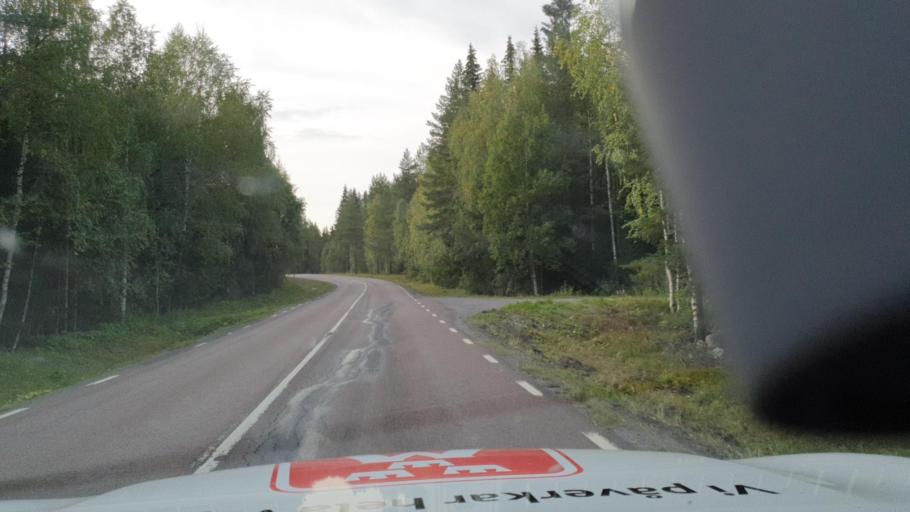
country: SE
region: Jaemtland
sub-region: Stroemsunds Kommun
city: Stroemsund
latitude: 63.8095
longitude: 15.6768
